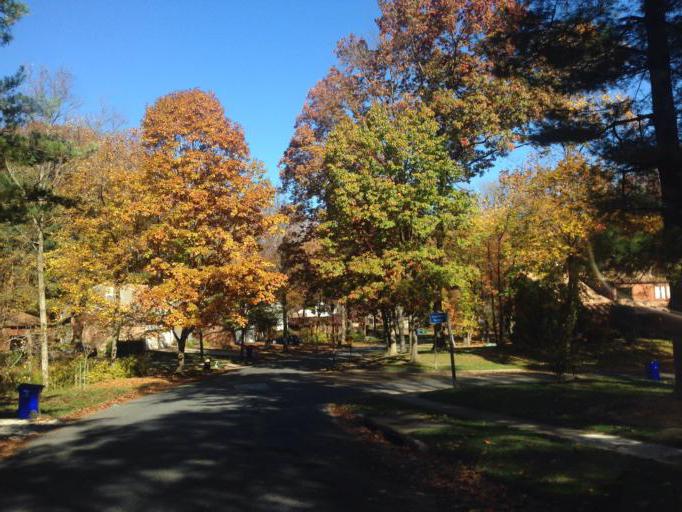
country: US
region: Maryland
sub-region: Howard County
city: Riverside
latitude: 39.1947
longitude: -76.8796
